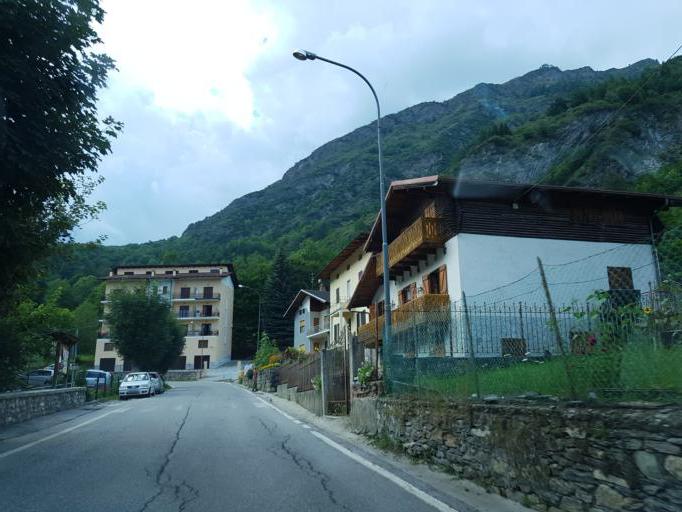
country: IT
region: Piedmont
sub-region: Provincia di Cuneo
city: Prazzo Superiore
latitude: 44.4828
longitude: 7.0540
